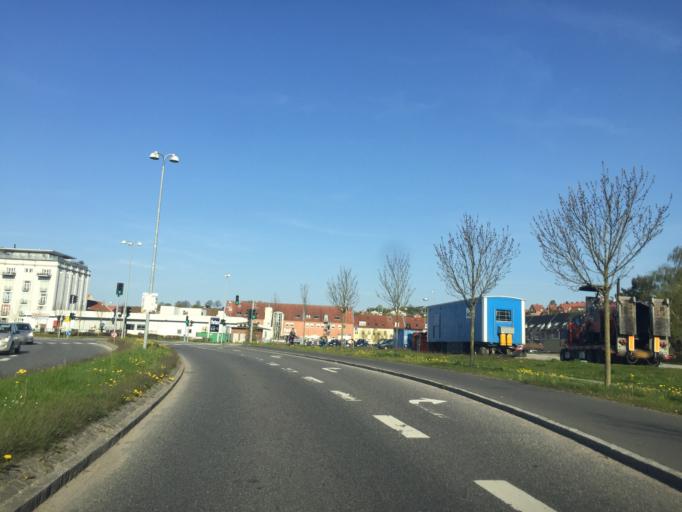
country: DK
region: South Denmark
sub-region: Svendborg Kommune
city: Svendborg
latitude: 55.0636
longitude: 10.6171
